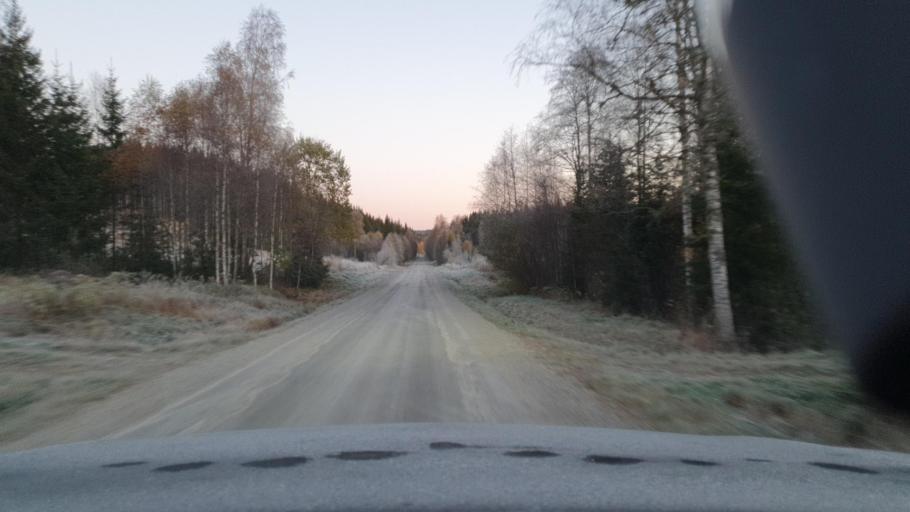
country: SE
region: Vaermland
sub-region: Arvika Kommun
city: Arvika
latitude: 59.8017
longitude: 12.7492
